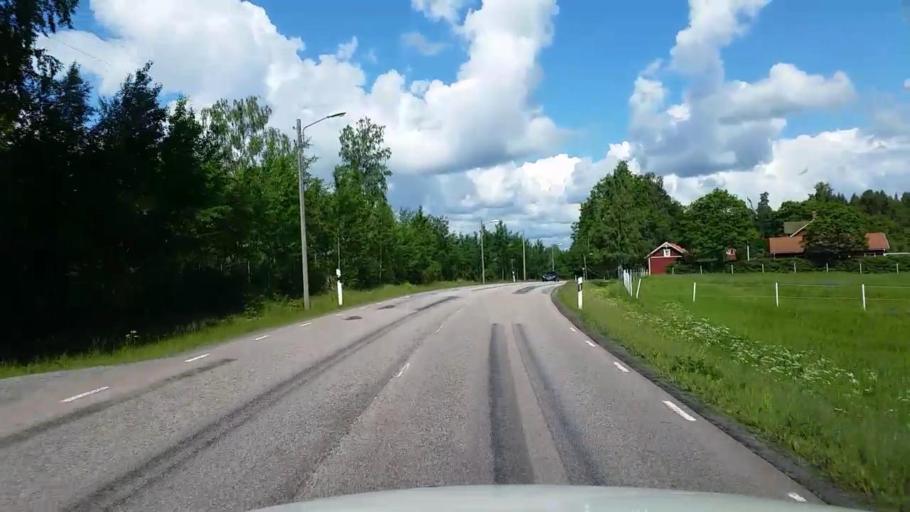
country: SE
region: Vaestmanland
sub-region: Kopings Kommun
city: Kolsva
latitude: 59.6289
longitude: 15.8072
